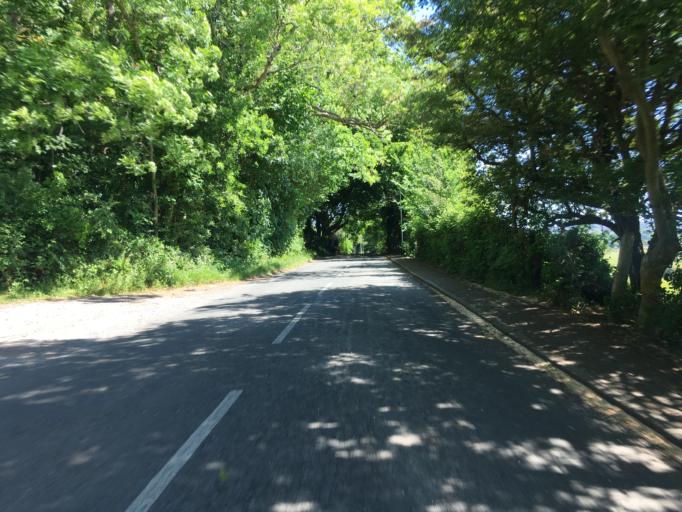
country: GB
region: England
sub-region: South Gloucestershire
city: Winterbourne
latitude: 51.5158
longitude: -2.5076
